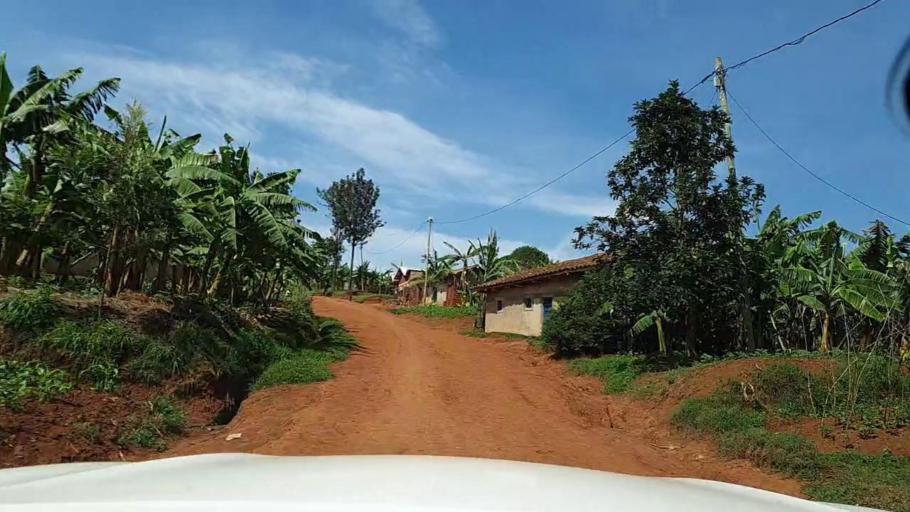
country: RW
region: Southern Province
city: Butare
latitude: -2.7000
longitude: 29.8514
